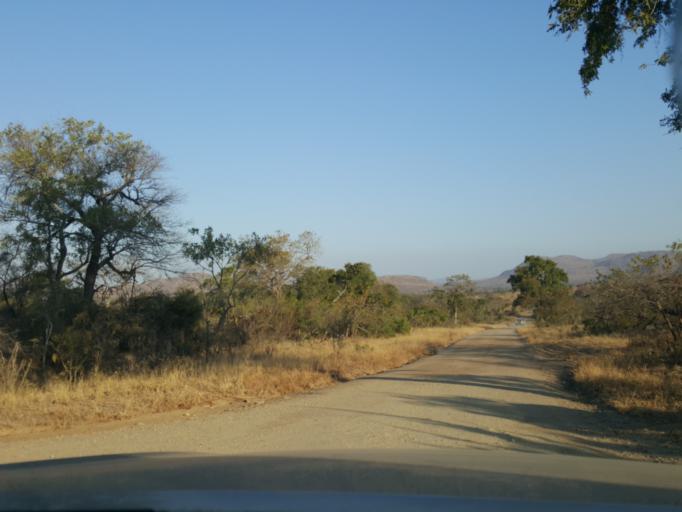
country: SZ
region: Hhohho
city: Ntfonjeni
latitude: -25.4131
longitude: 31.4408
